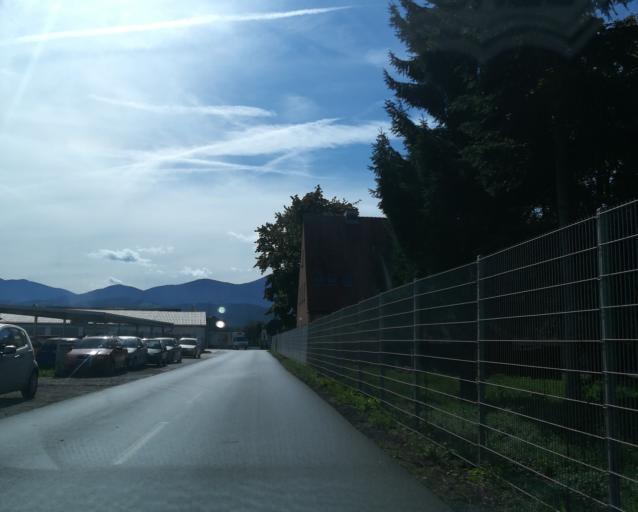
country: AT
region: Styria
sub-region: Politischer Bezirk Murtal
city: Zeltweg
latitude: 47.1981
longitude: 14.7643
